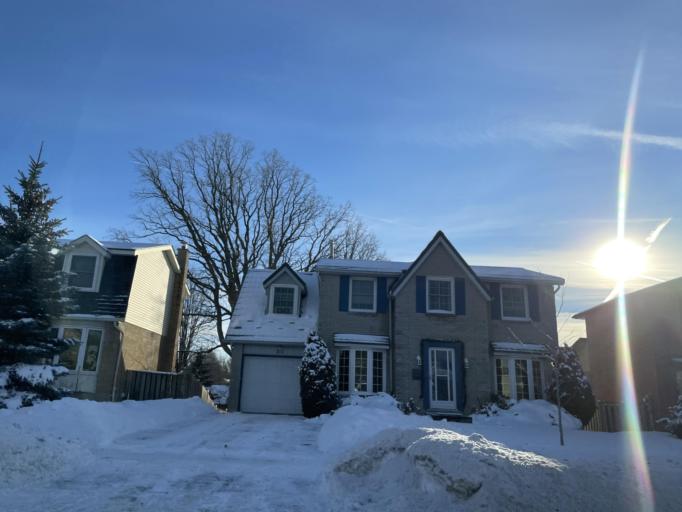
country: CA
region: Ontario
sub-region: Wellington County
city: Guelph
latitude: 43.5132
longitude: -80.2358
